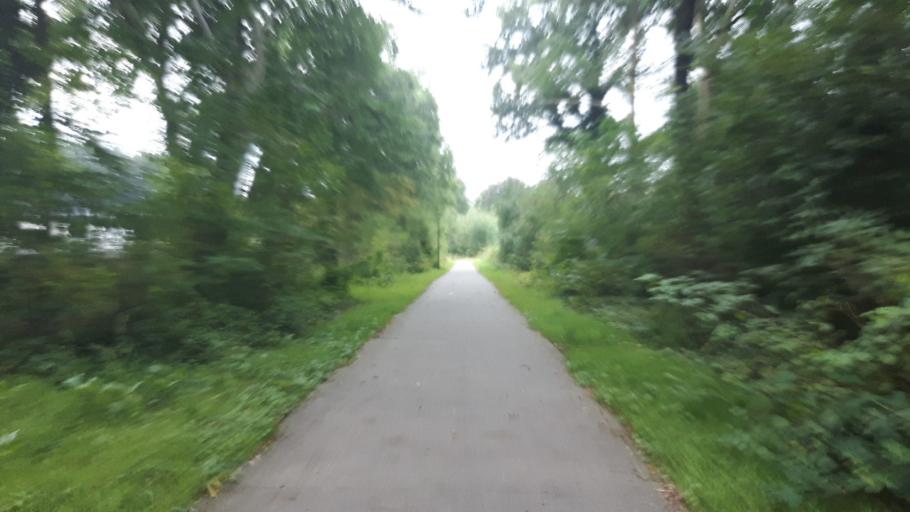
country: NL
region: Friesland
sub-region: Gemeente Heerenveen
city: Jubbega
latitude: 52.9894
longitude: 6.2805
